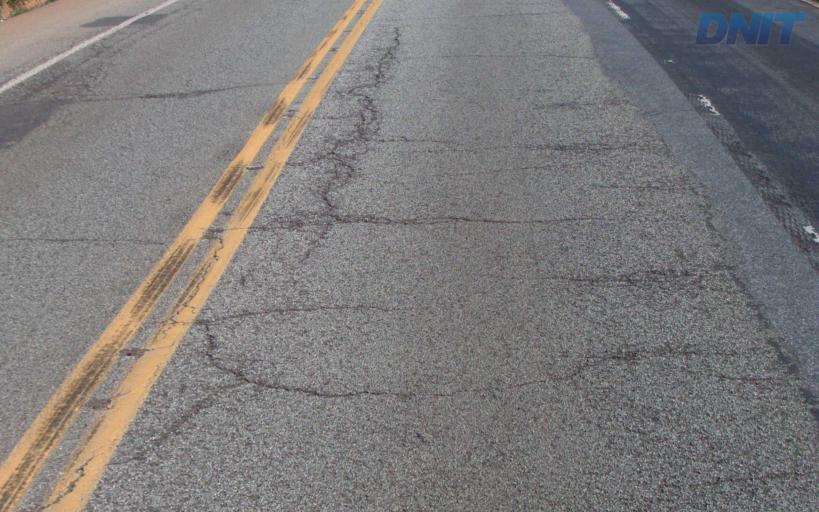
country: BR
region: Minas Gerais
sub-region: Caete
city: Caete
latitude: -19.7488
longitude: -43.5441
